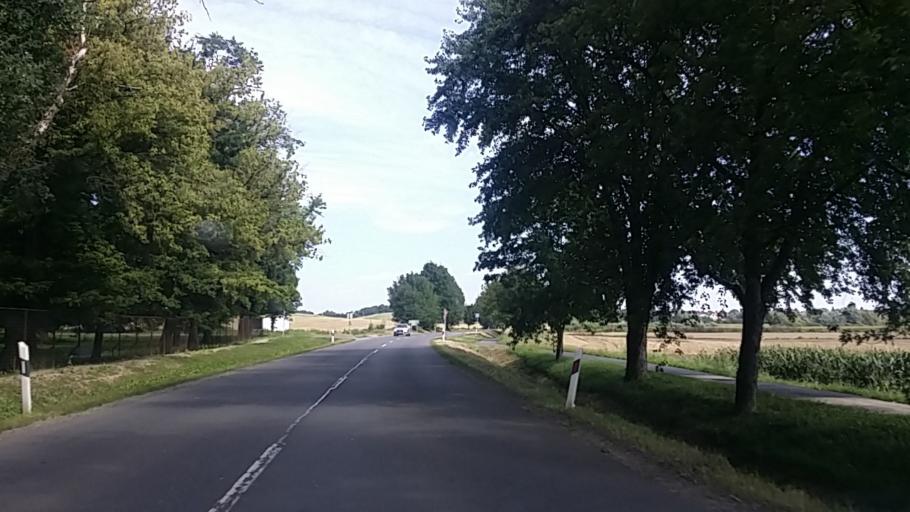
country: HU
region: Baranya
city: Sasd
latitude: 46.2931
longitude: 18.1219
